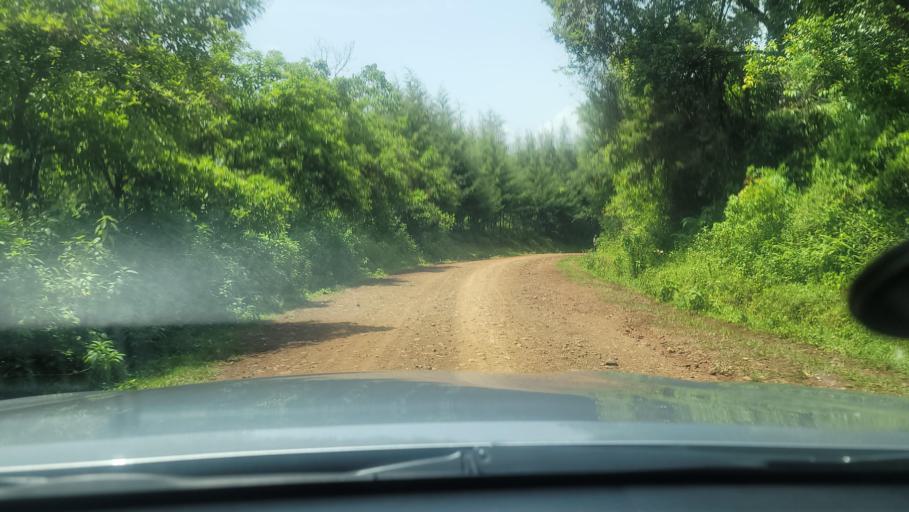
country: ET
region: Oromiya
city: Agaro
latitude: 7.8057
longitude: 36.4148
